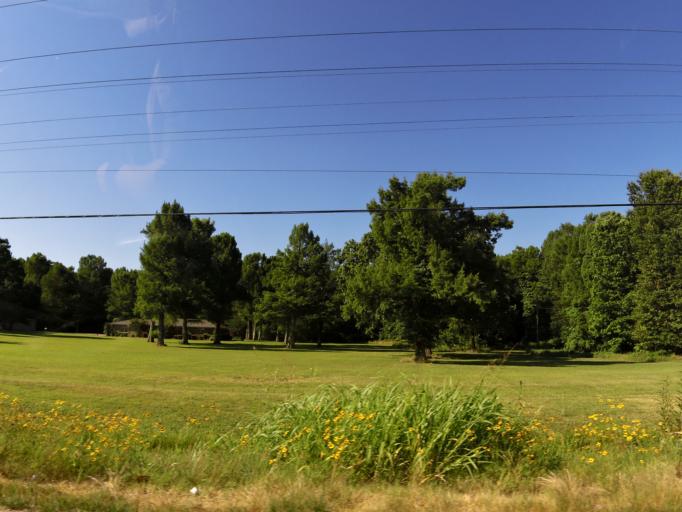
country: US
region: Arkansas
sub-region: Clay County
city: Corning
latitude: 36.4067
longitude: -90.5760
